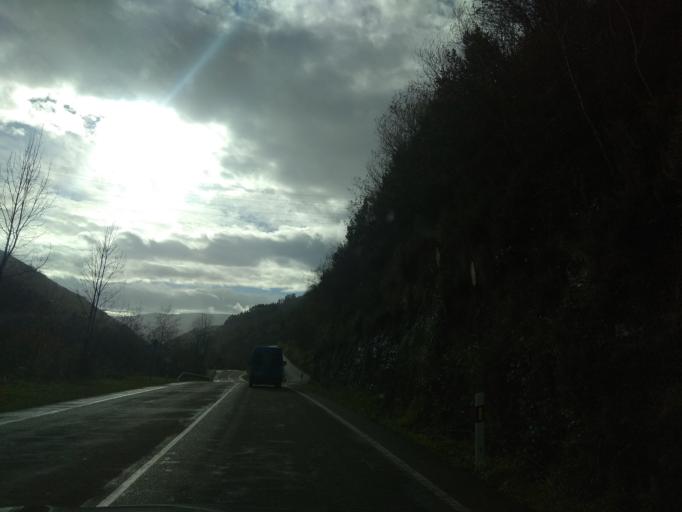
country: ES
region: Cantabria
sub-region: Provincia de Cantabria
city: San Pedro del Romeral
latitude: 43.1503
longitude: -3.8979
